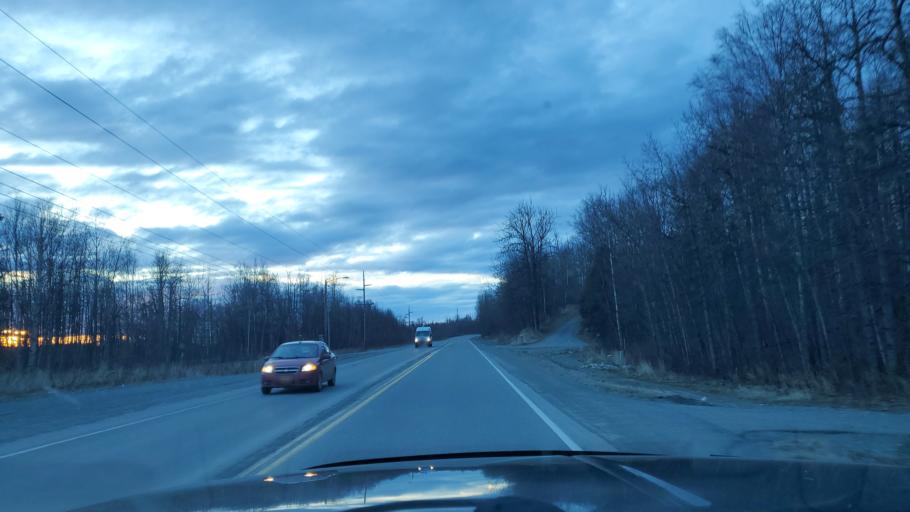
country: US
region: Alaska
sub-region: Matanuska-Susitna Borough
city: Lakes
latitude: 61.6076
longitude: -149.3364
